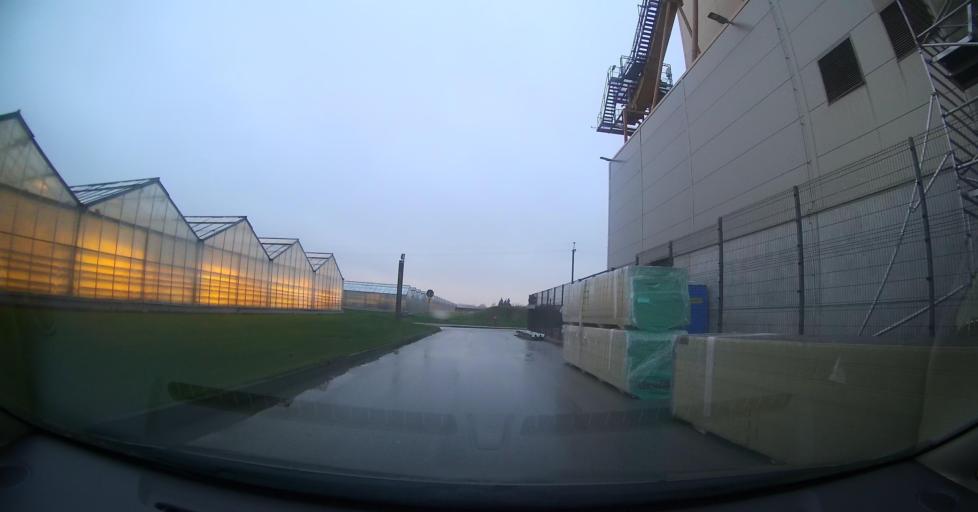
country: EE
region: Tartu
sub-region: Tartu linn
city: Tartu
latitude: 58.3693
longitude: 26.7910
